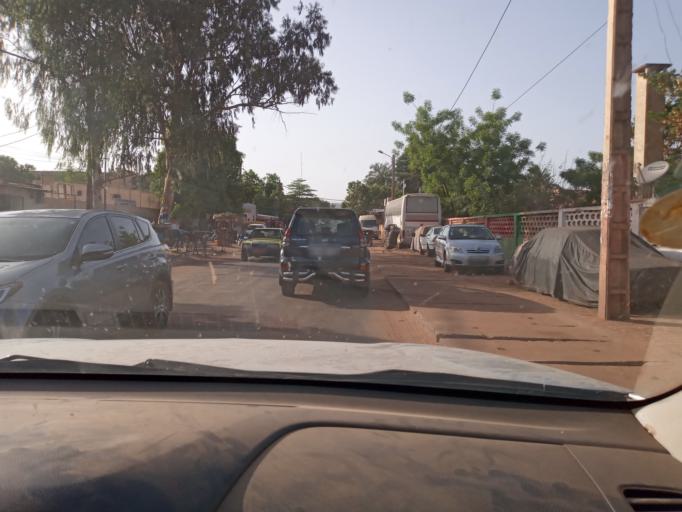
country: ML
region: Bamako
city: Bamako
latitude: 12.6583
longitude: -7.9714
